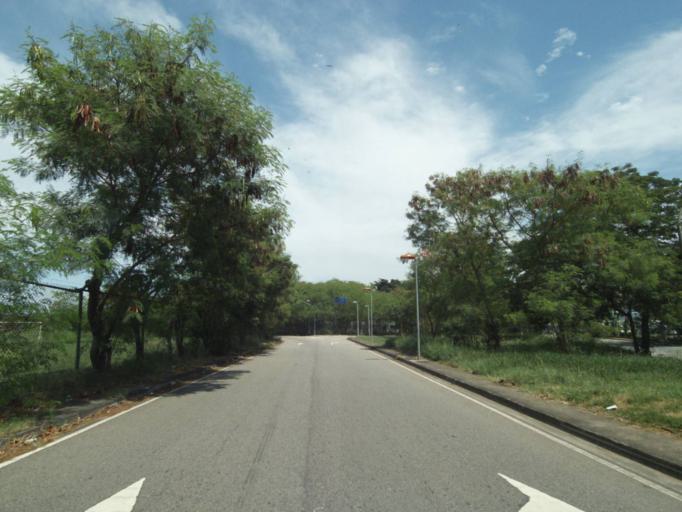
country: BR
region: Rio de Janeiro
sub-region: Rio De Janeiro
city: Rio de Janeiro
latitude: -22.8317
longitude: -43.2448
